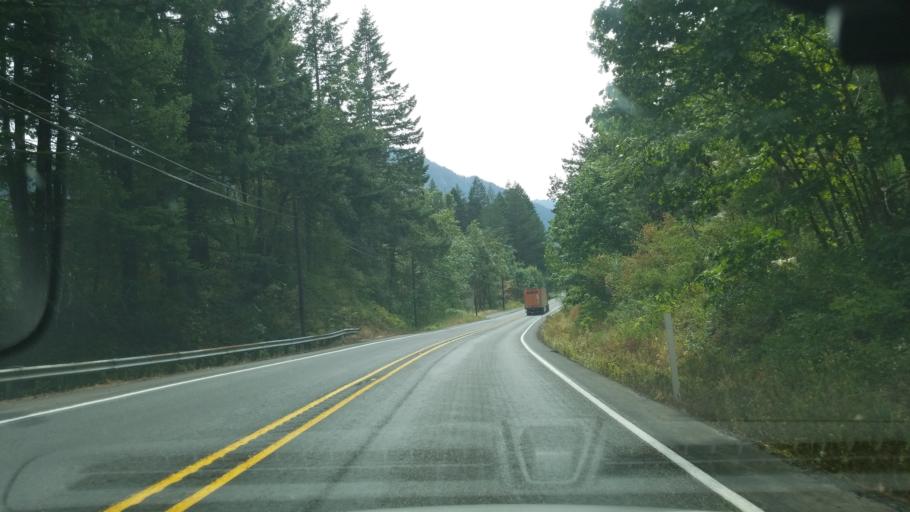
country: US
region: Oregon
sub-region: Hood River County
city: Cascade Locks
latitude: 45.6580
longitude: -121.9083
